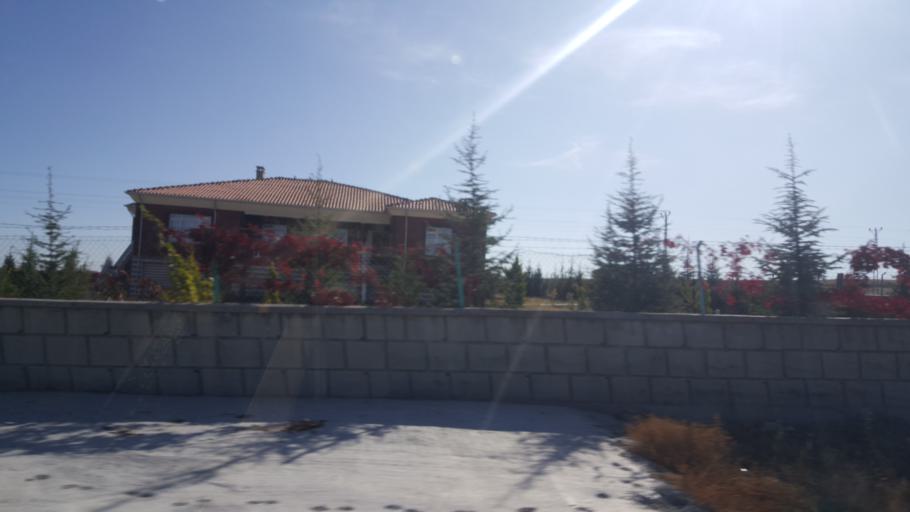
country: TR
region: Ankara
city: Altpinar
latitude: 39.2404
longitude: 32.7382
